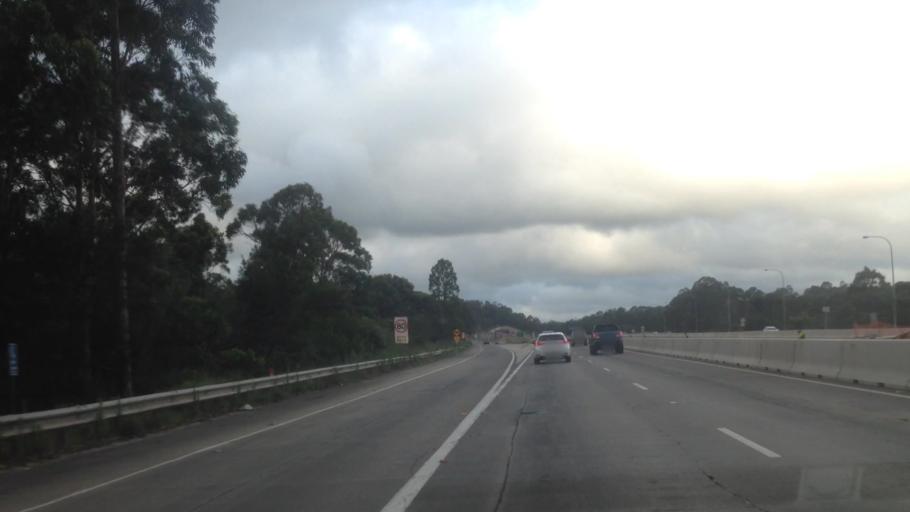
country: AU
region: New South Wales
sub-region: Wyong Shire
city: Jilliby
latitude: -33.2217
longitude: 151.4339
